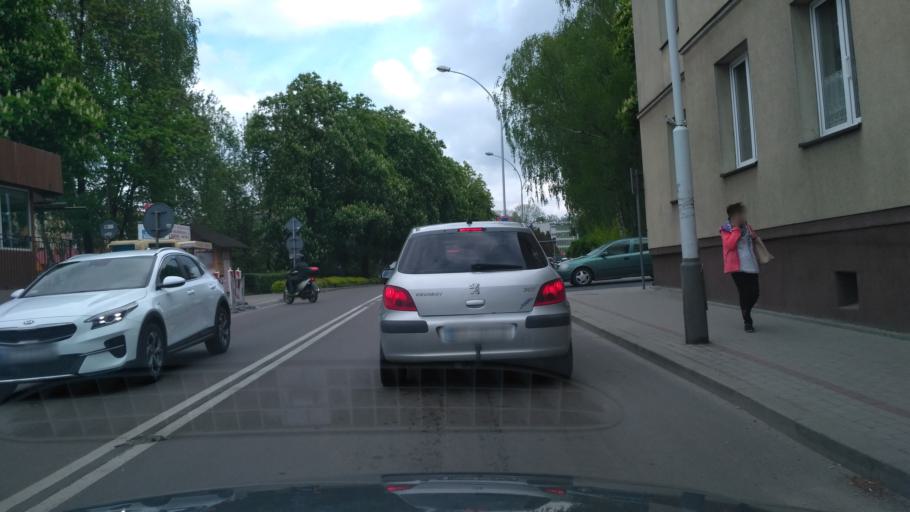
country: PL
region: Subcarpathian Voivodeship
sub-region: Powiat przeworski
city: Przeworsk
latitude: 50.0575
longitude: 22.4930
